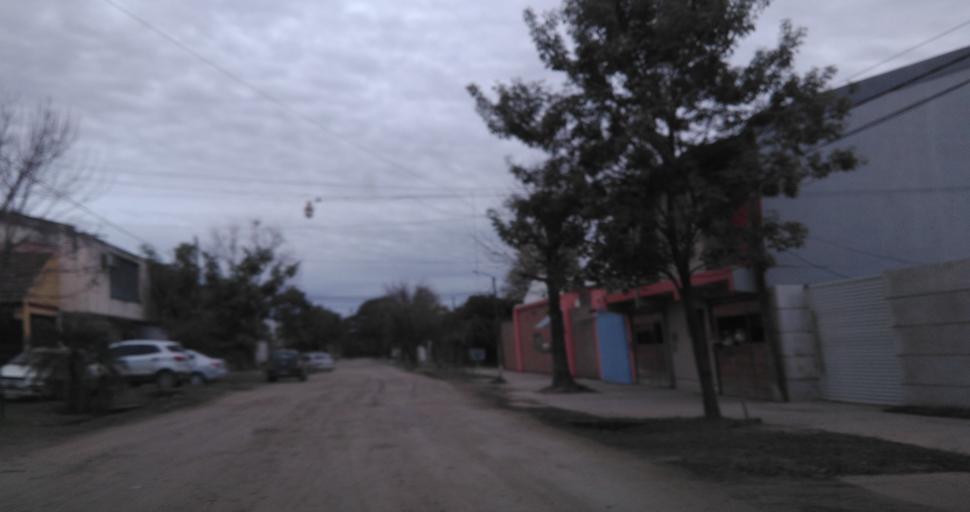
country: AR
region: Chaco
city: Resistencia
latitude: -27.4653
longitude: -58.9724
